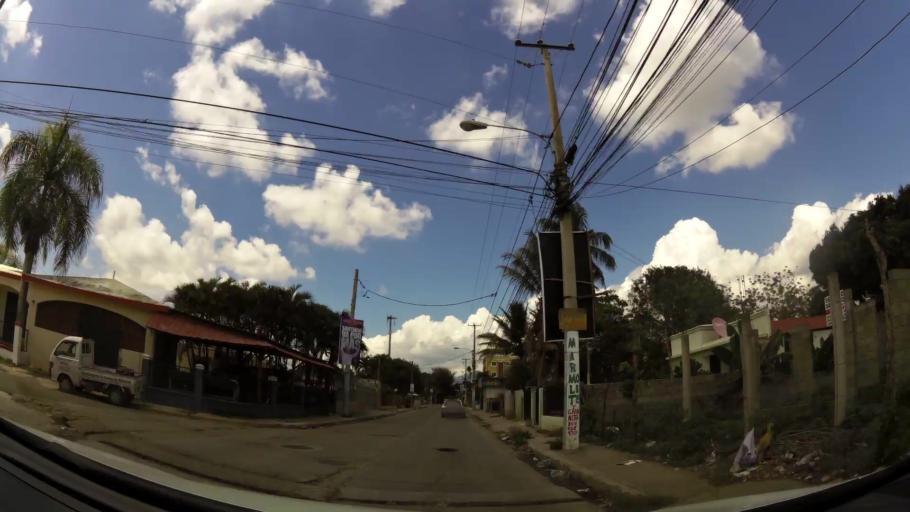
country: DO
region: Santiago
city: Santiago de los Caballeros
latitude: 19.4741
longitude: -70.6675
